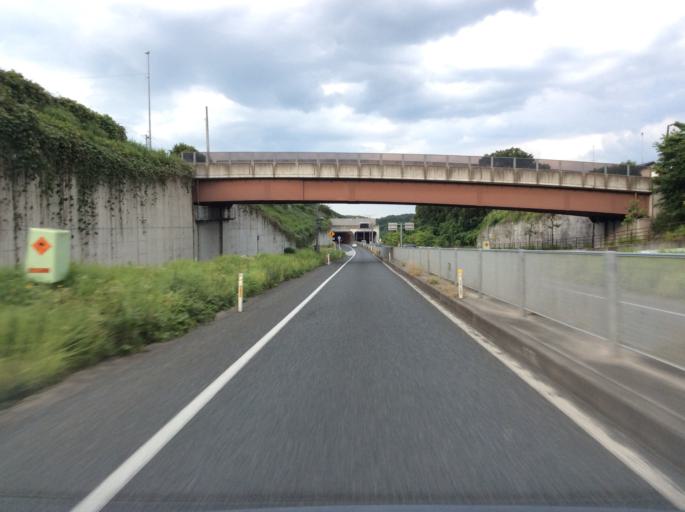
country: JP
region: Fukushima
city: Iwaki
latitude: 37.0306
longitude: 140.9049
